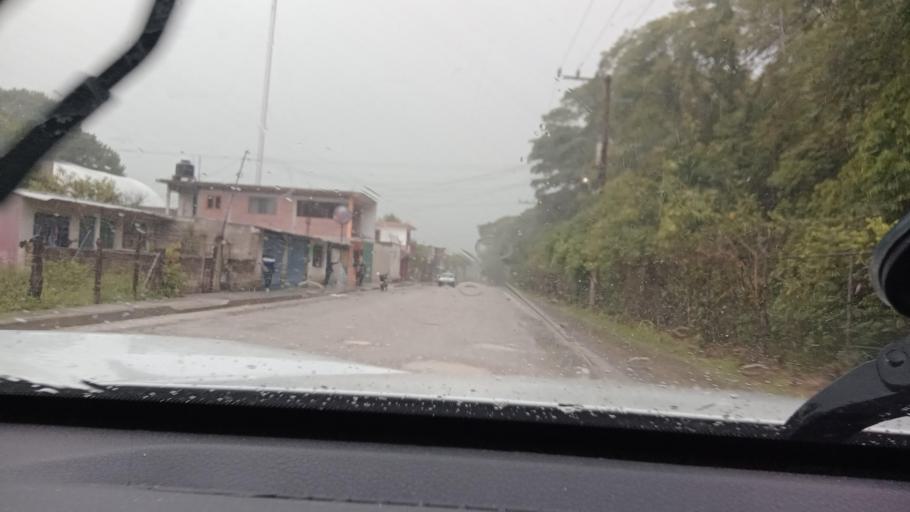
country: MX
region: Veracruz
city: Coatepec
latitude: 19.4575
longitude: -96.9776
